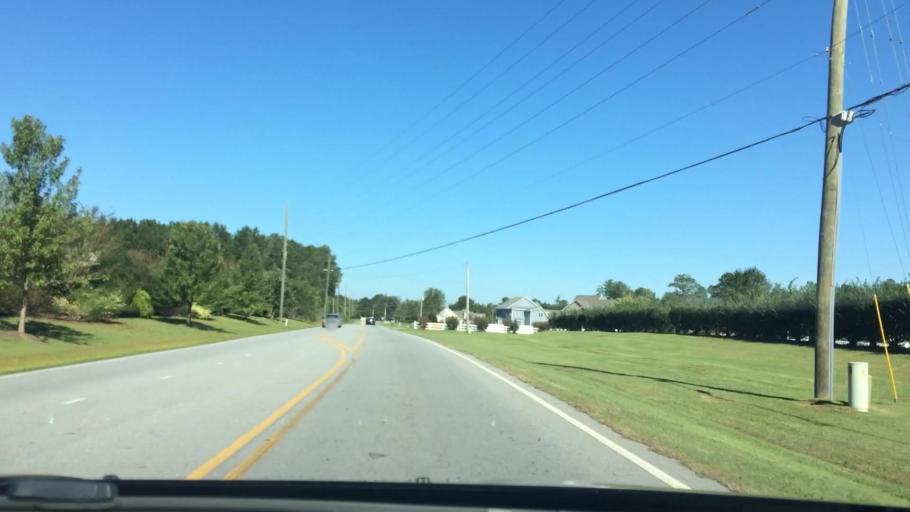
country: US
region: North Carolina
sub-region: Pitt County
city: Summerfield
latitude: 35.5573
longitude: -77.4441
